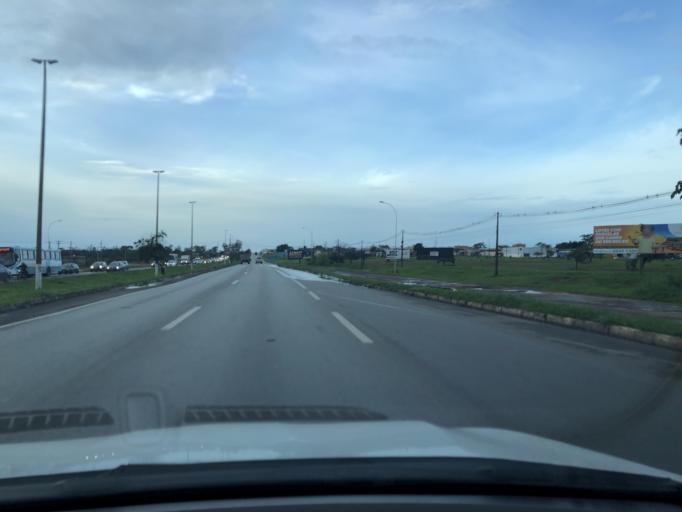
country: BR
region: Federal District
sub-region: Brasilia
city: Brasilia
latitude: -16.0063
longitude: -47.9837
